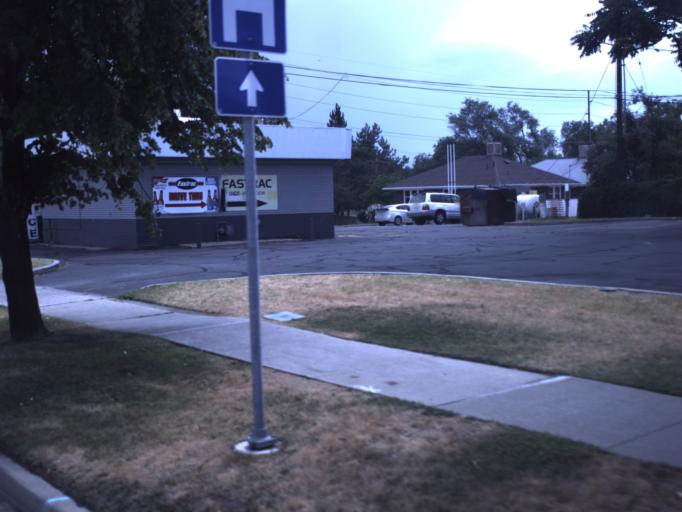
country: US
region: Utah
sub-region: Salt Lake County
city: South Salt Lake
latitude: 40.7134
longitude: -111.8715
